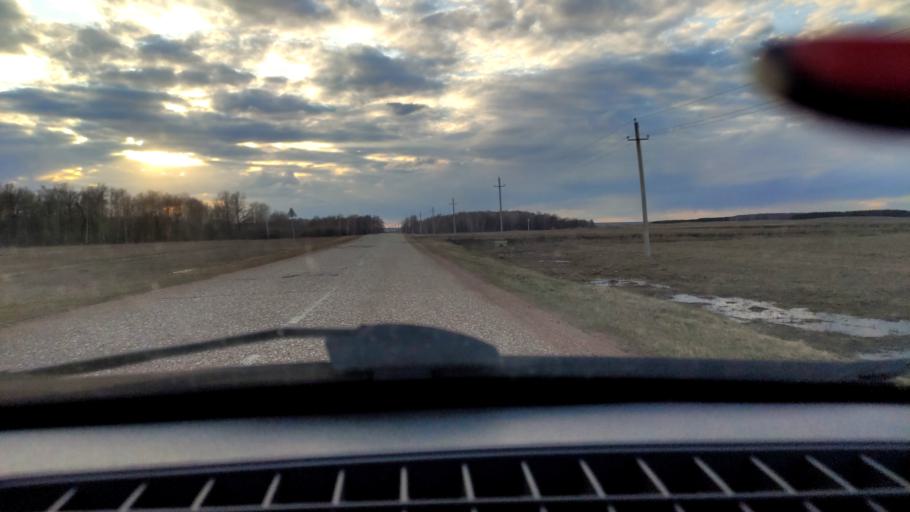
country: RU
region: Bashkortostan
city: Tolbazy
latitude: 54.0042
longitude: 55.6142
